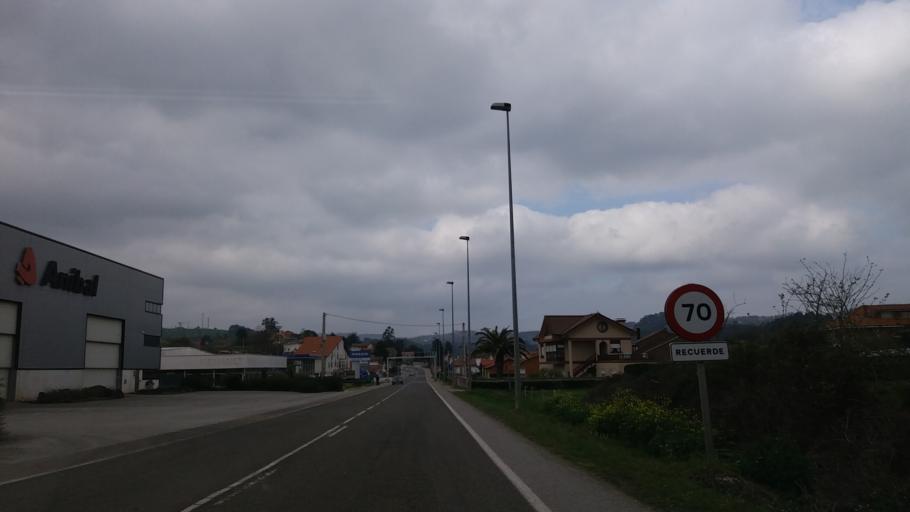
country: ES
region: Cantabria
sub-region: Provincia de Cantabria
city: Reocin
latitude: 43.3553
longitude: -4.1093
